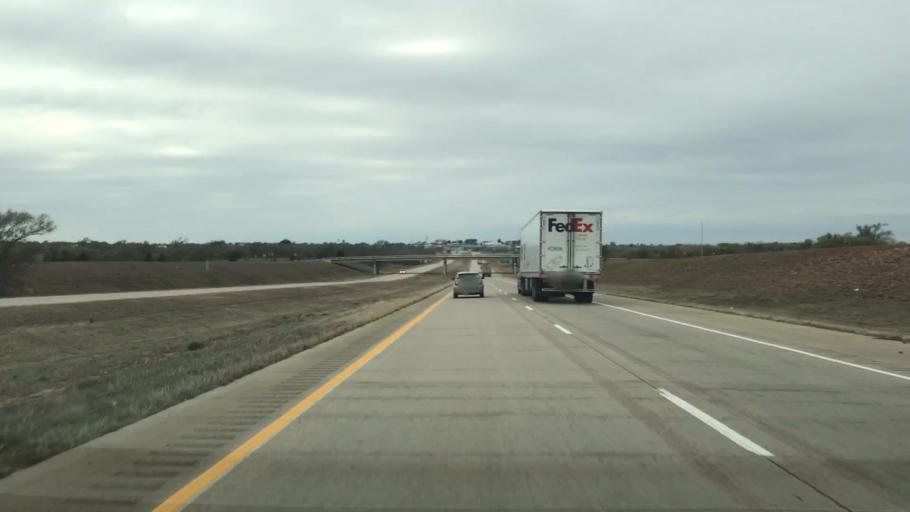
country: US
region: Texas
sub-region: Wheeler County
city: Shamrock
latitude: 35.2275
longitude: -100.2232
